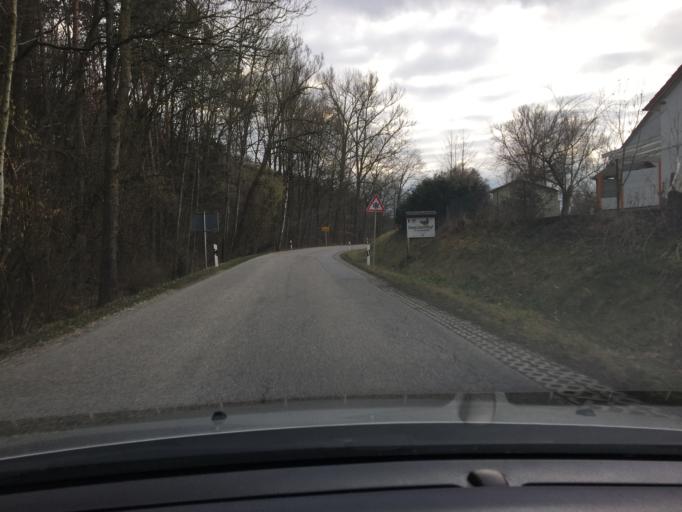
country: DE
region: Bavaria
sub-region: Lower Bavaria
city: Kumhausen
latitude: 48.5090
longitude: 12.1555
